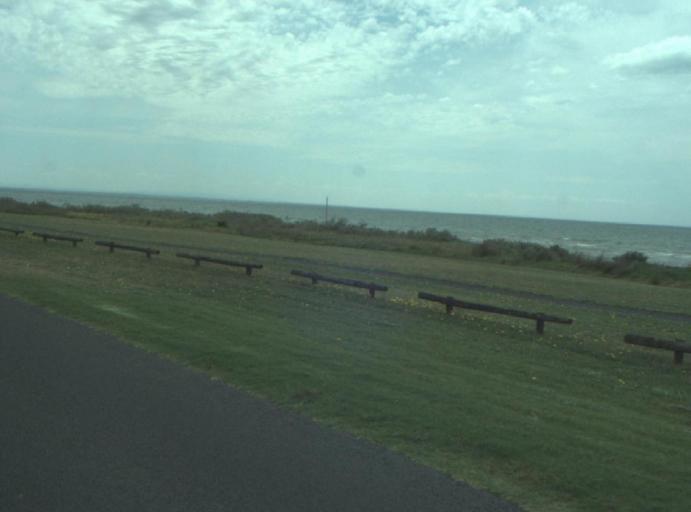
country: AU
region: Victoria
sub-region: Greater Geelong
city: Clifton Springs
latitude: -38.1231
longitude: 144.6946
